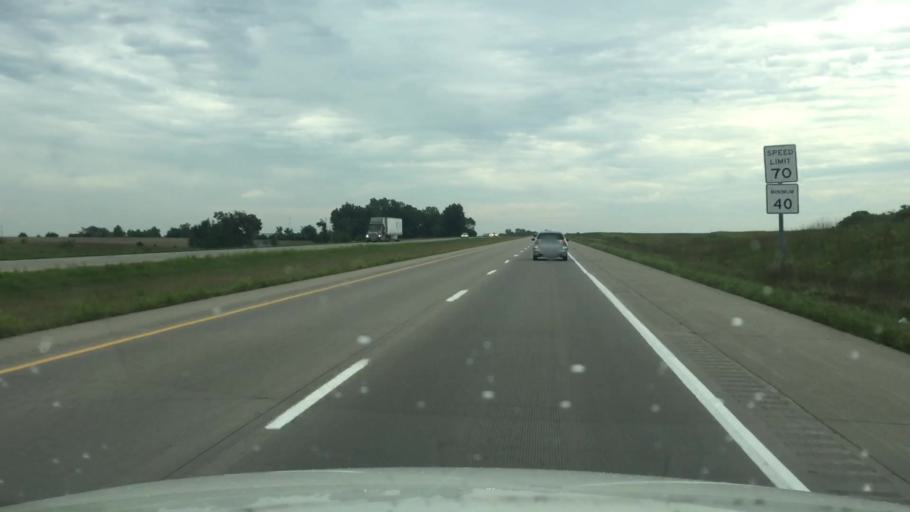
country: US
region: Iowa
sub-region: Clarke County
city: Osceola
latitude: 40.9617
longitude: -93.7982
